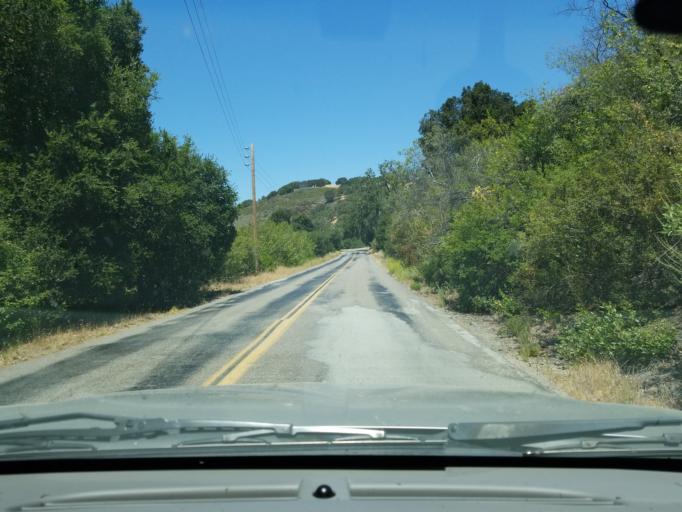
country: US
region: California
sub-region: Monterey County
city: Carmel Valley Village
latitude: 36.4338
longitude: -121.6286
